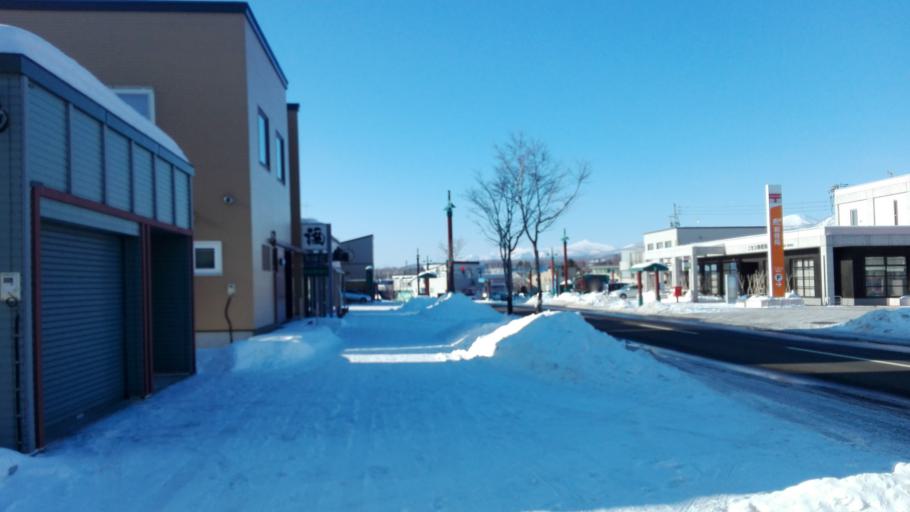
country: JP
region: Hokkaido
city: Niseko Town
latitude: 42.8037
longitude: 140.6867
